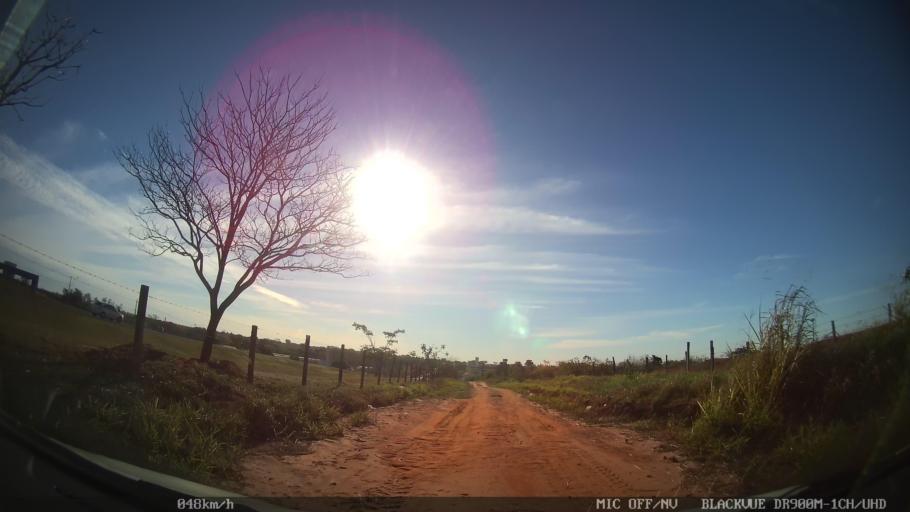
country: BR
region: Sao Paulo
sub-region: Sao Jose Do Rio Preto
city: Sao Jose do Rio Preto
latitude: -20.8752
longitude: -49.3214
